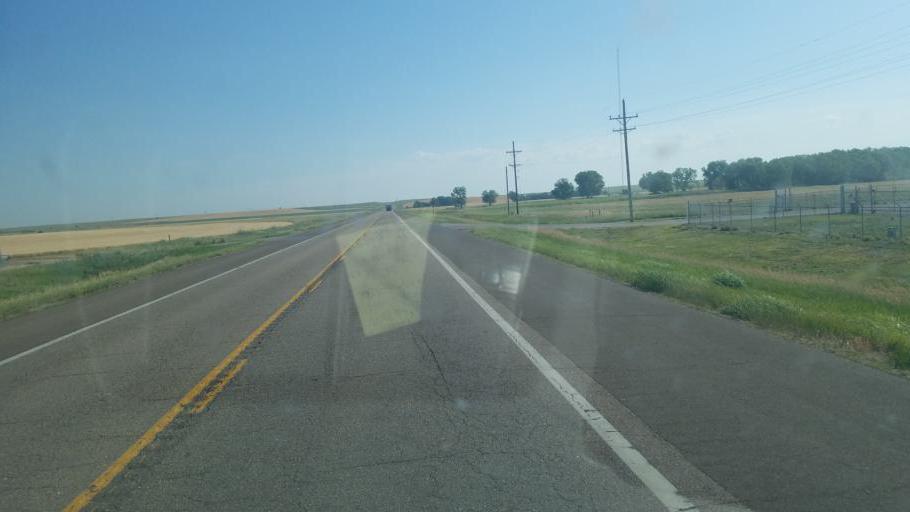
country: US
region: Kansas
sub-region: Barton County
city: Great Bend
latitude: 38.3692
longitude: -98.6926
